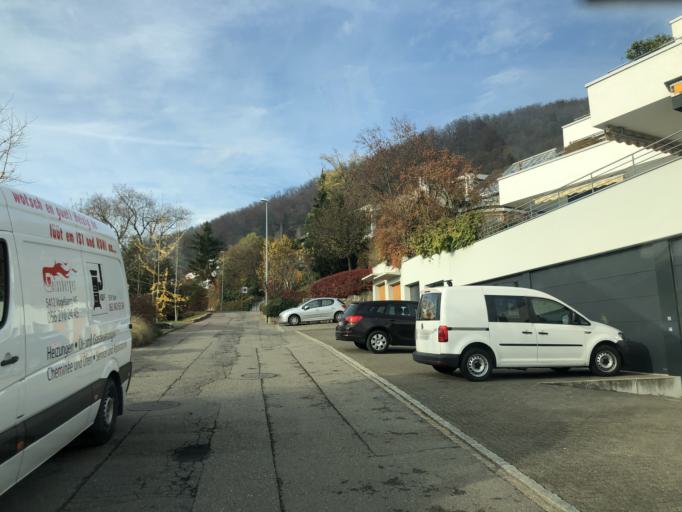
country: CH
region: Aargau
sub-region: Bezirk Baden
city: Wettingen
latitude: 47.4713
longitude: 8.3271
